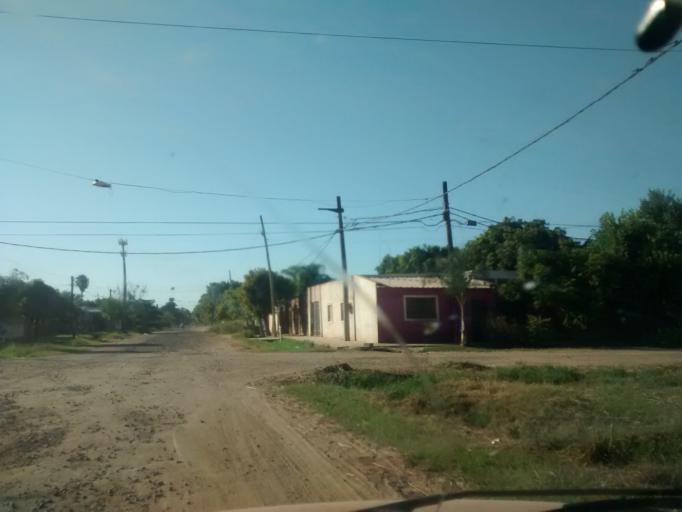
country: AR
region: Chaco
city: Resistencia
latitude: -27.4482
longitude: -58.9686
